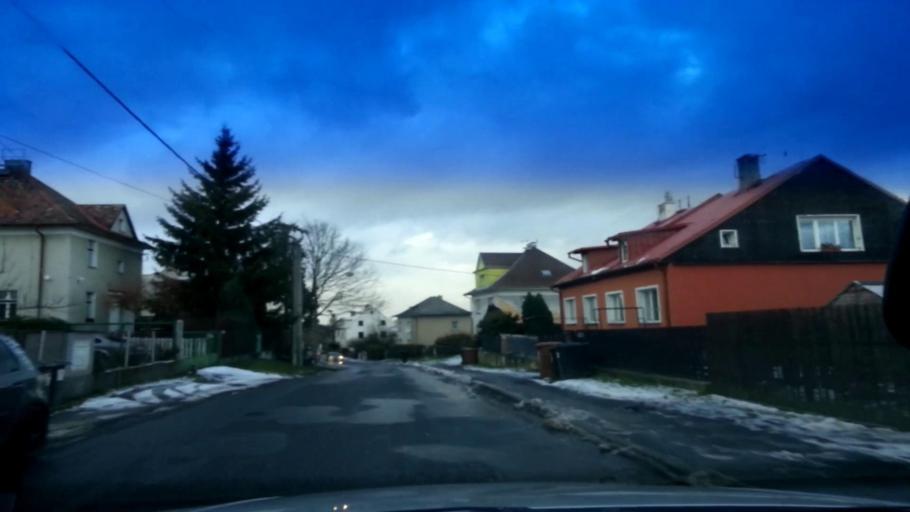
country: CZ
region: Karlovarsky
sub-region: Okres Cheb
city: Cheb
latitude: 50.0606
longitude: 12.3715
